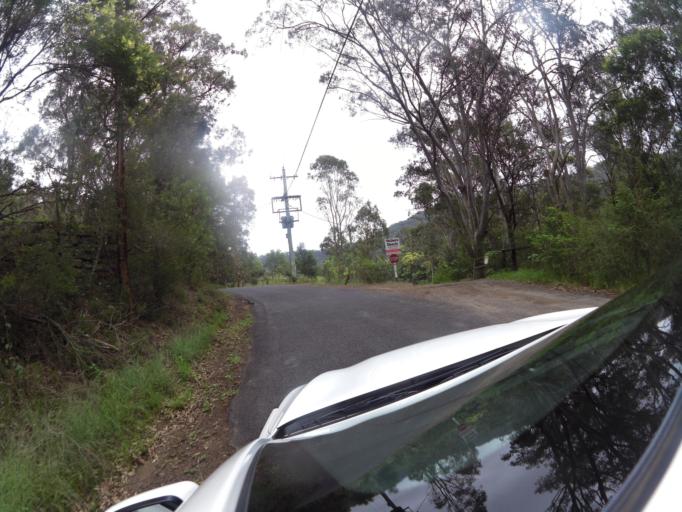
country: AU
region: New South Wales
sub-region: Hornsby Shire
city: Glenorie
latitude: -33.4157
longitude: 150.9560
